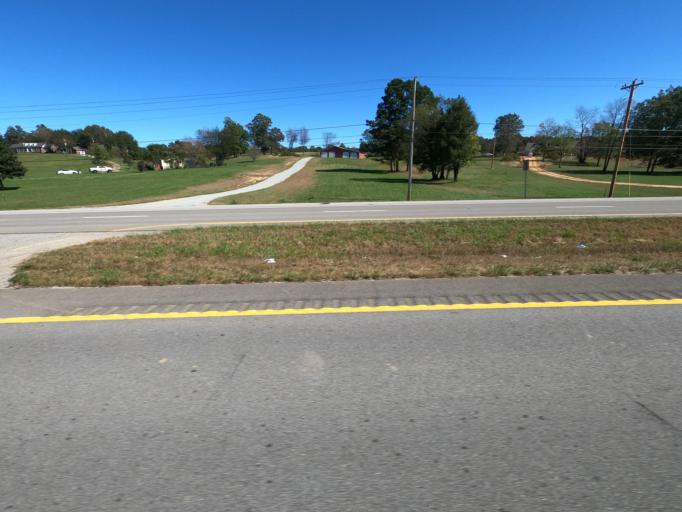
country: US
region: Tennessee
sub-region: Maury County
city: Mount Pleasant
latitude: 35.3956
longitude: -87.2780
